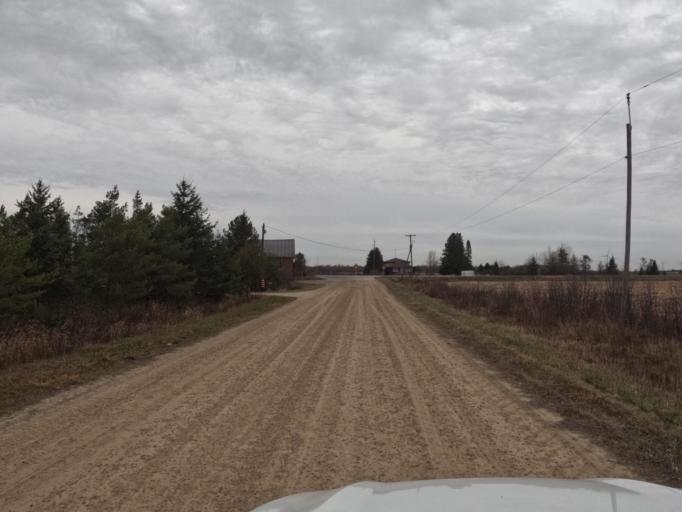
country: CA
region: Ontario
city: Shelburne
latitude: 44.0386
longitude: -80.3730
